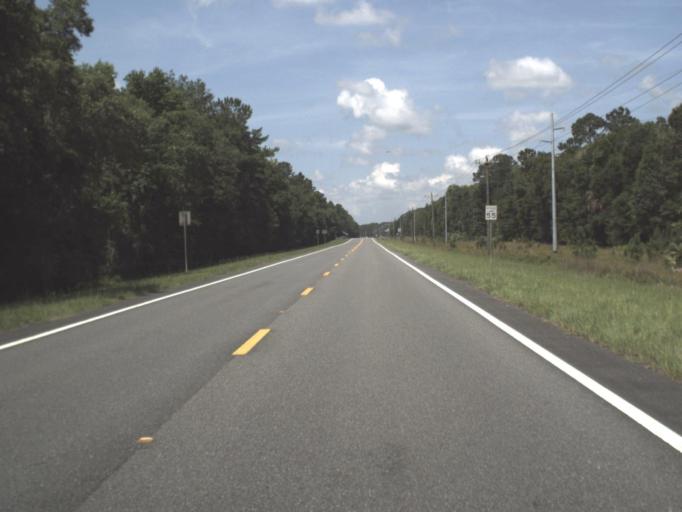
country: US
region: Florida
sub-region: Levy County
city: Chiefland
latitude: 29.3210
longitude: -82.7805
